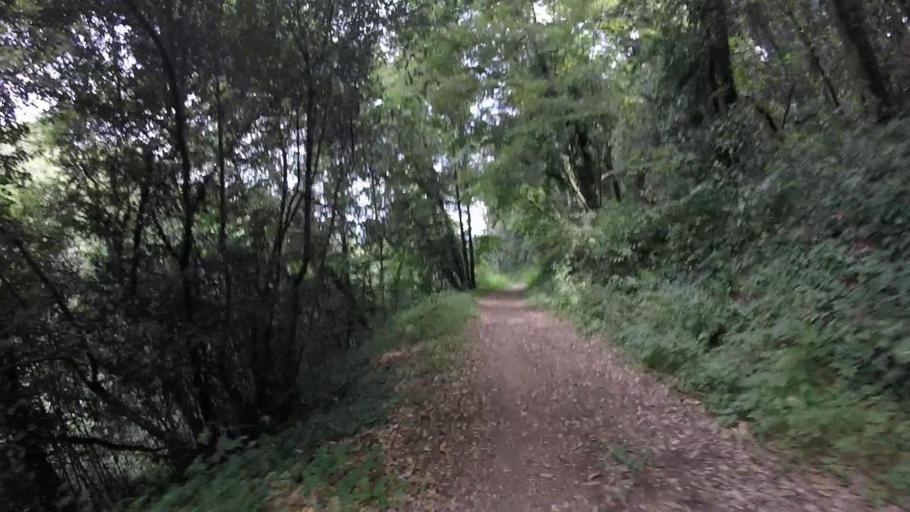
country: FR
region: Provence-Alpes-Cote d'Azur
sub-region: Departement des Alpes-Maritimes
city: Biot
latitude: 43.6153
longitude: 7.0907
